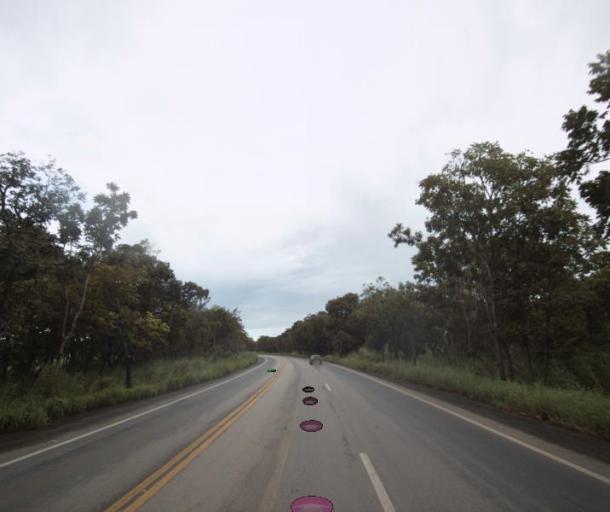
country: BR
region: Goias
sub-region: Porangatu
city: Porangatu
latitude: -13.7433
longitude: -49.0308
